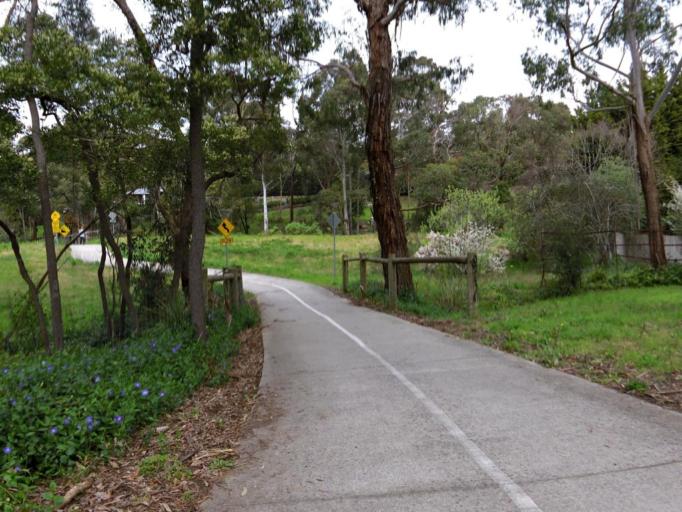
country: AU
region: Victoria
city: Mitcham
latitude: -37.8034
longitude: 145.2018
